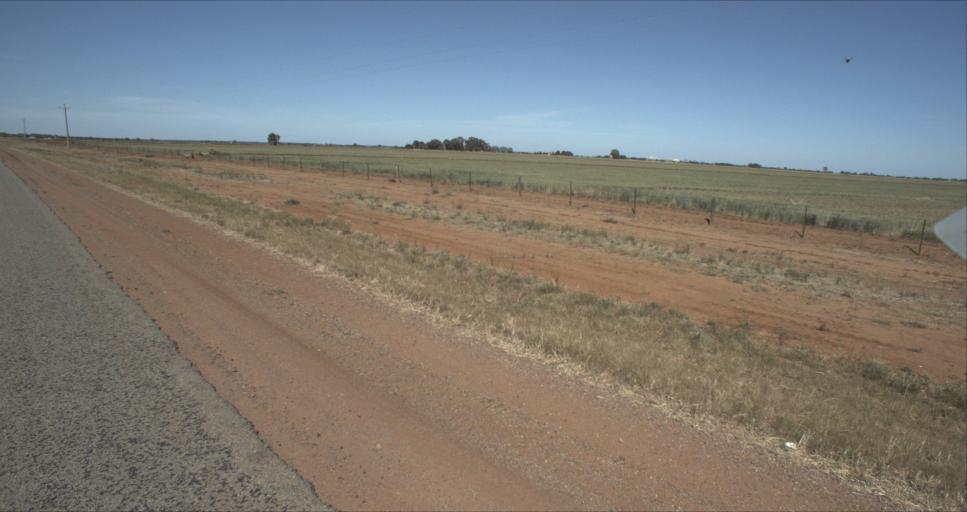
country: AU
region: New South Wales
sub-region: Leeton
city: Leeton
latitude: -34.5469
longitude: 146.3154
